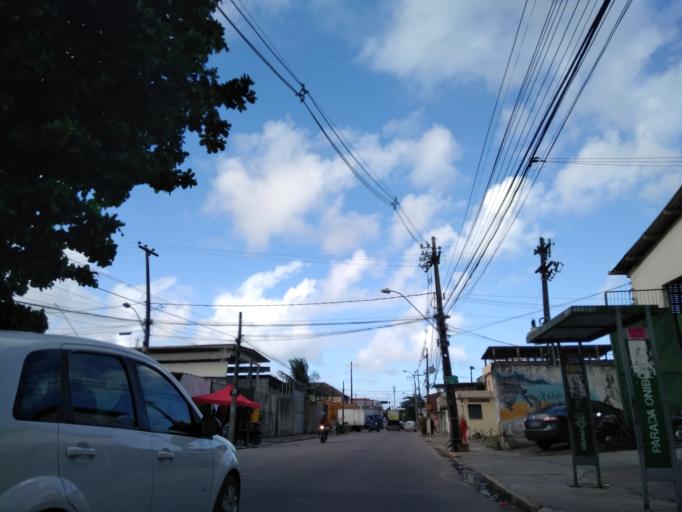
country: BR
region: Pernambuco
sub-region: Recife
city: Recife
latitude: -8.0750
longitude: -34.9199
